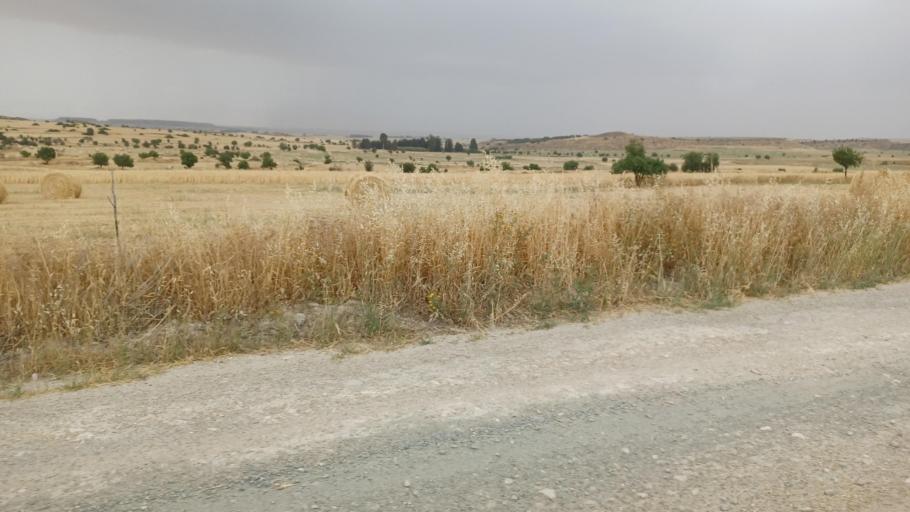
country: CY
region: Larnaka
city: Athienou
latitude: 35.0411
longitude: 33.5737
